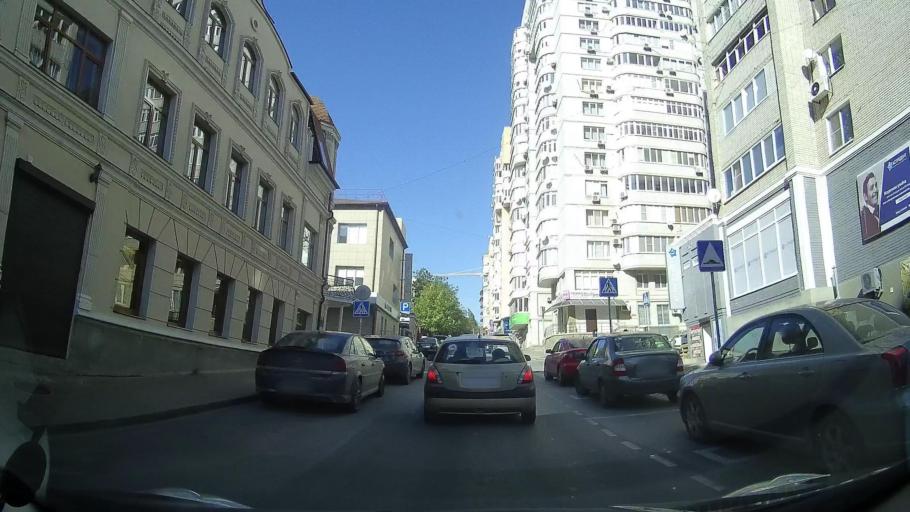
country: RU
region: Rostov
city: Rostov-na-Donu
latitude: 47.2199
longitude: 39.6995
